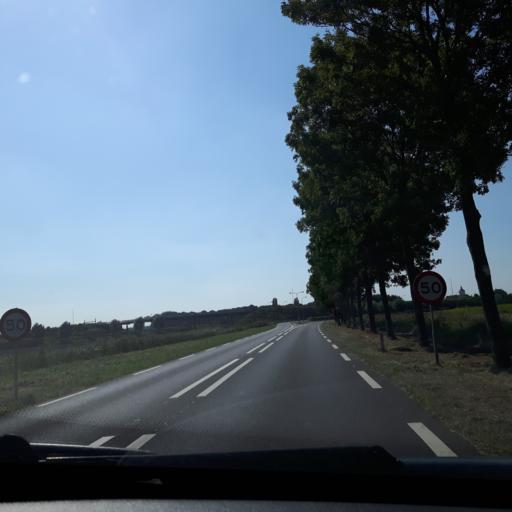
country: NL
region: Zeeland
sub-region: Gemeente Goes
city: Goes
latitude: 51.4924
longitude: 3.9293
